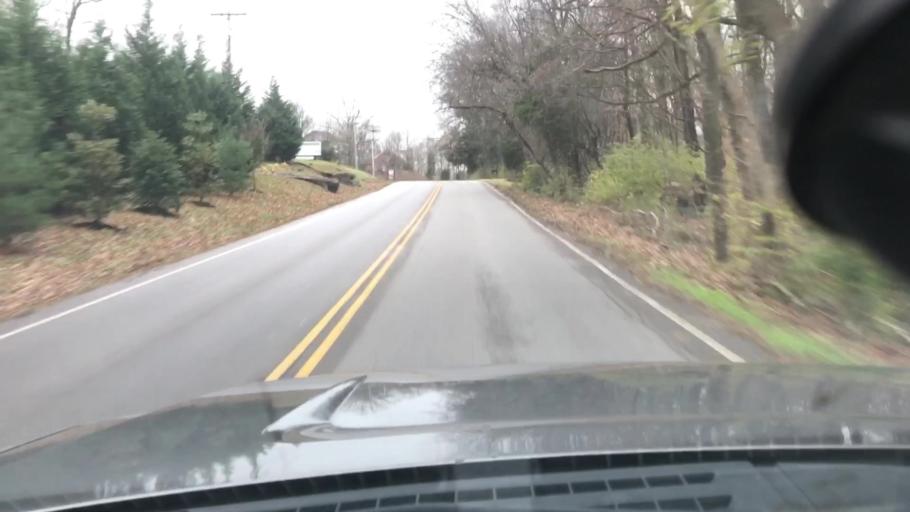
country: US
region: Tennessee
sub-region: Williamson County
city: Brentwood Estates
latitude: 35.9810
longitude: -86.7451
